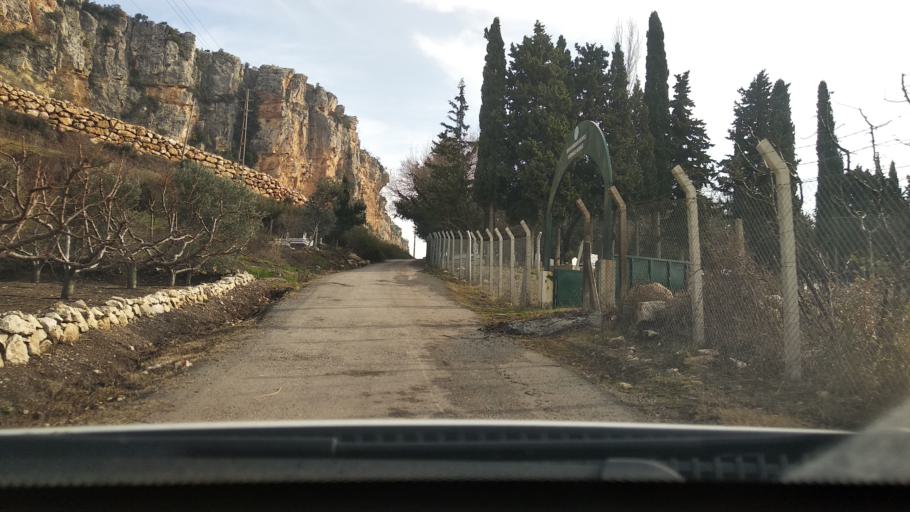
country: TR
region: Mersin
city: Kuzucubelen
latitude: 36.8762
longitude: 34.4719
